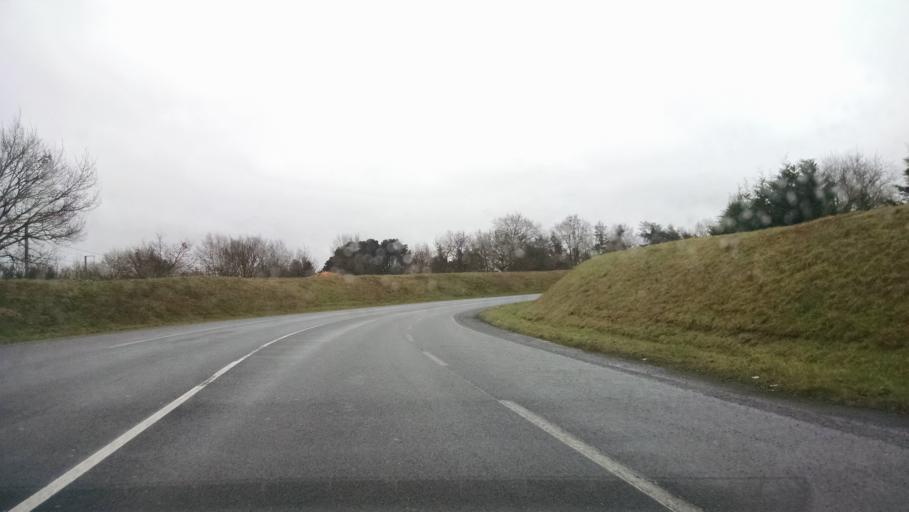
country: FR
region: Pays de la Loire
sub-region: Departement de la Loire-Atlantique
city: Gorges
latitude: 47.0932
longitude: -1.2970
